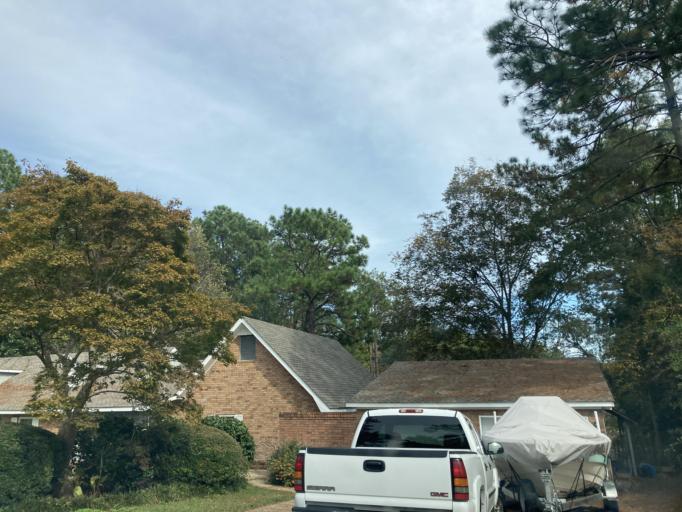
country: US
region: Mississippi
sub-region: Lamar County
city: West Hattiesburg
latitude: 31.3215
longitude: -89.4324
